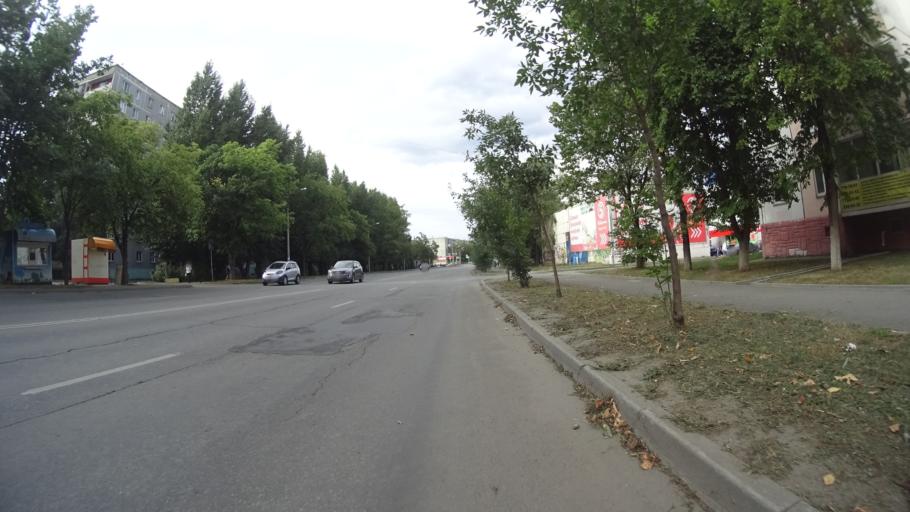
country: RU
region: Chelyabinsk
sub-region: Gorod Chelyabinsk
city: Chelyabinsk
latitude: 55.1970
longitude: 61.3179
